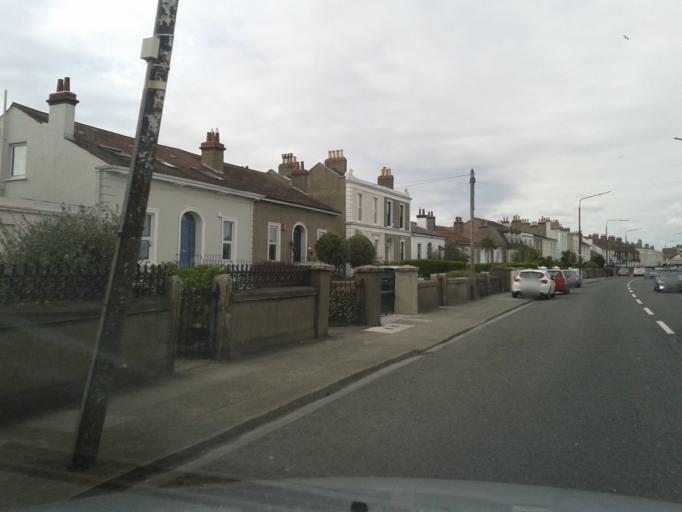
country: IE
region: Leinster
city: Sandymount
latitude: 53.3265
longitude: -6.2081
